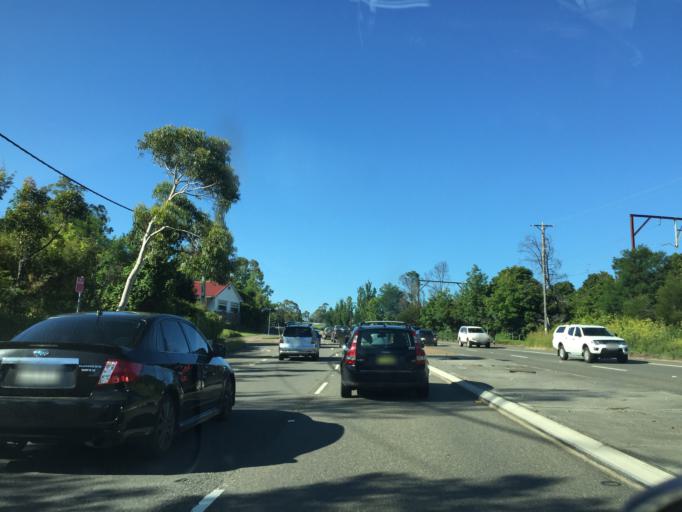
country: AU
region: New South Wales
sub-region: Blue Mountains Municipality
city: Hazelbrook
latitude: -33.6992
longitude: 150.5334
